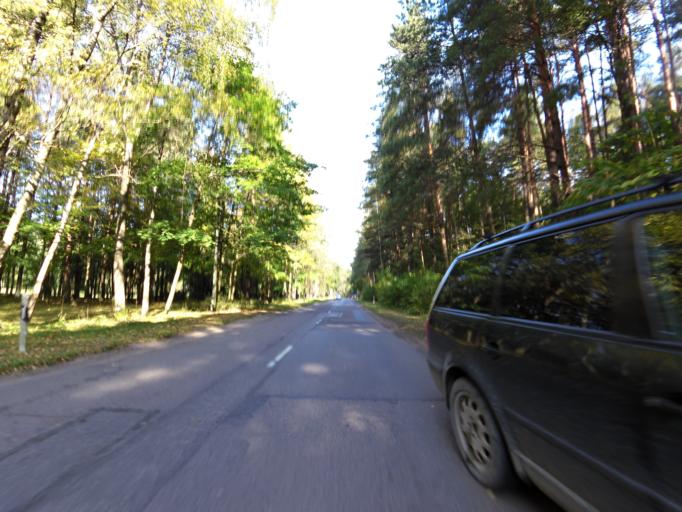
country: LT
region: Vilnius County
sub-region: Vilnius
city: Vilnius
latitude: 54.7368
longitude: 25.2944
